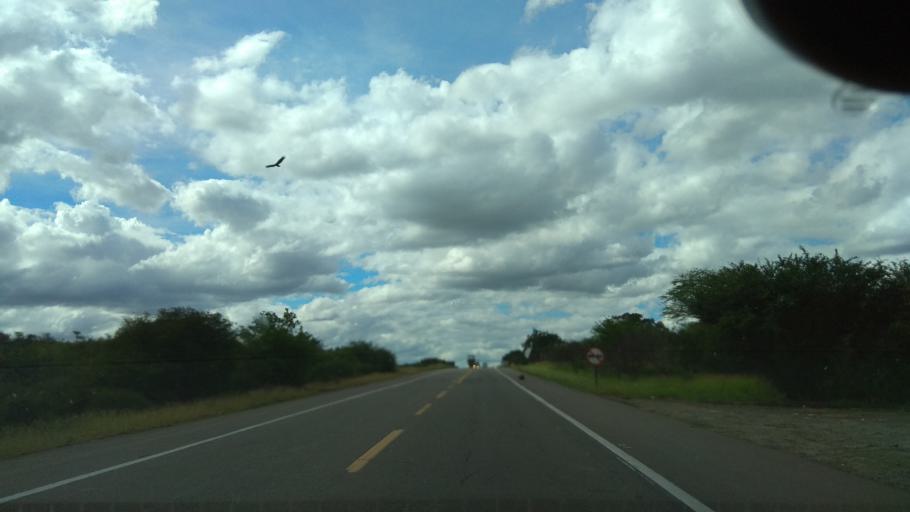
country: BR
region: Bahia
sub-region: Amargosa
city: Amargosa
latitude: -12.9763
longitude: -39.9376
